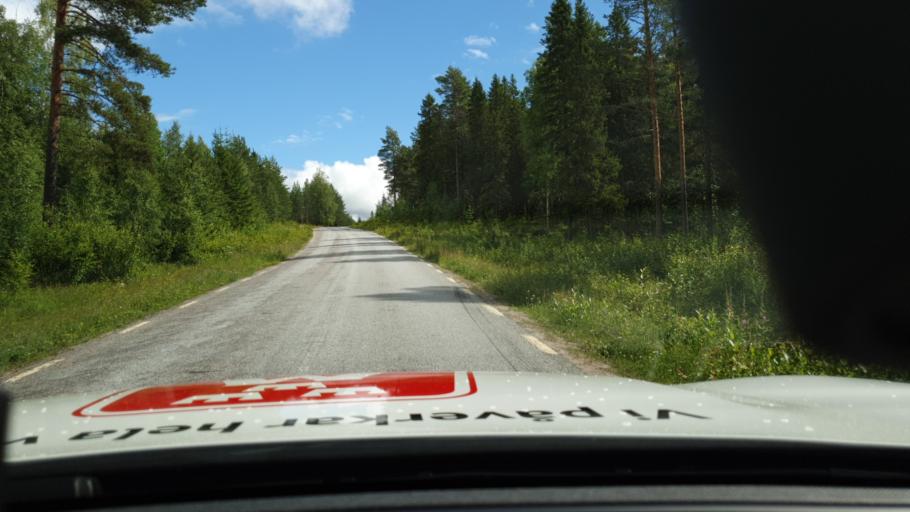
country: SE
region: Norrbotten
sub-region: Pitea Kommun
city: Rosvik
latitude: 65.4189
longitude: 21.7895
